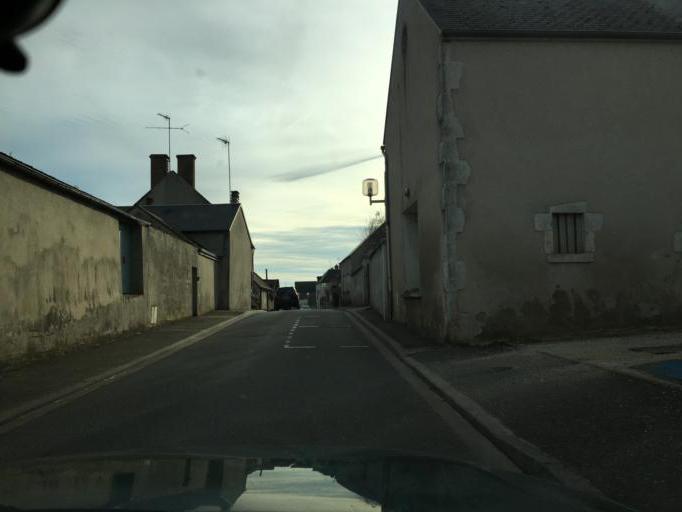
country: FR
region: Centre
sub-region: Departement du Loiret
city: Baule
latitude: 47.8134
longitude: 1.6822
